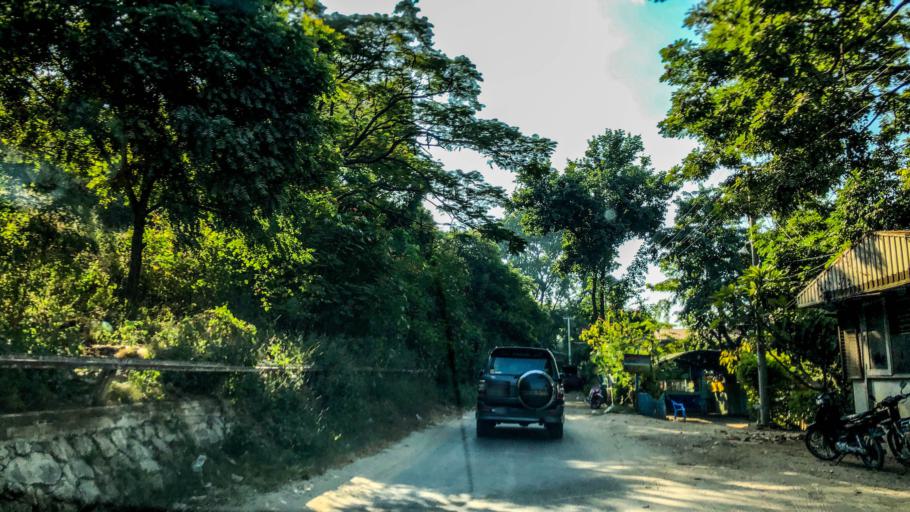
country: MM
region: Sagain
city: Sagaing
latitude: 21.8793
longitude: 95.9857
